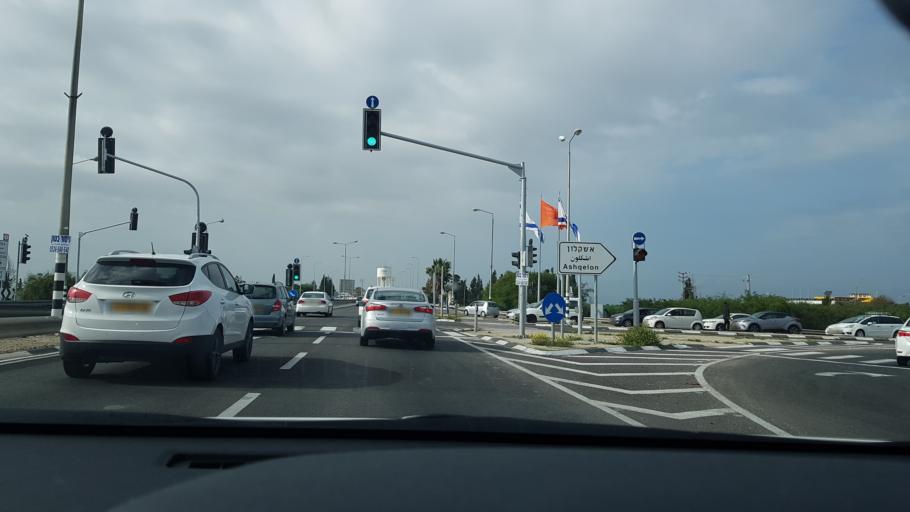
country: IL
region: Southern District
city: Ashqelon
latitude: 31.6591
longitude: 34.6030
